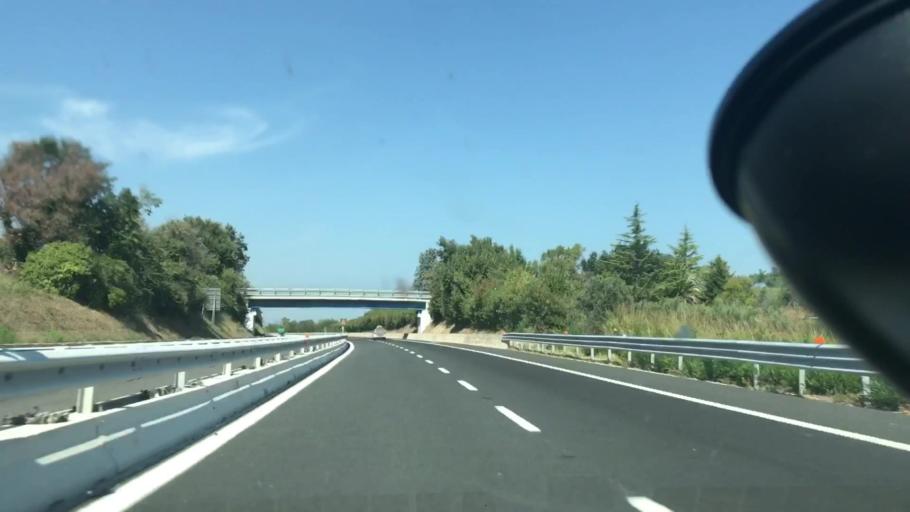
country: IT
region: Abruzzo
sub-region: Provincia di Chieti
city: Vasto
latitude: 42.1316
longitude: 14.6699
